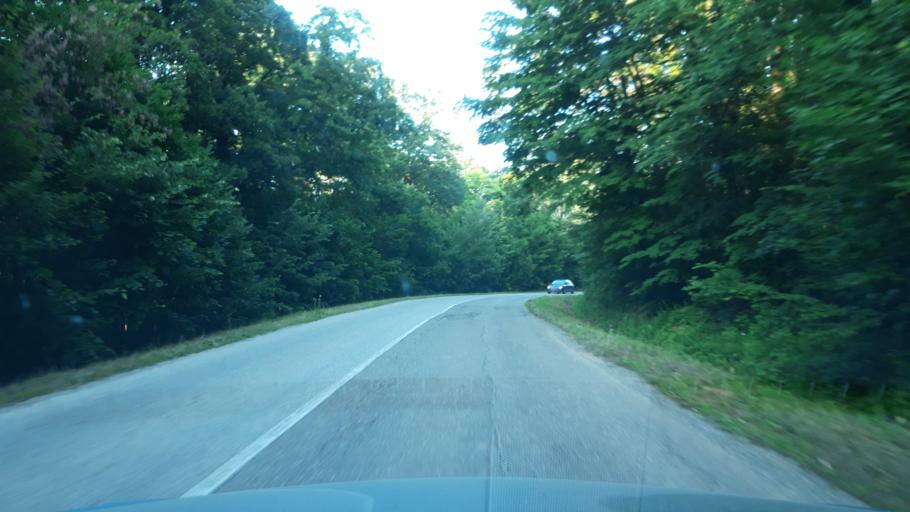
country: RS
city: Glozan
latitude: 45.1540
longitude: 19.5809
